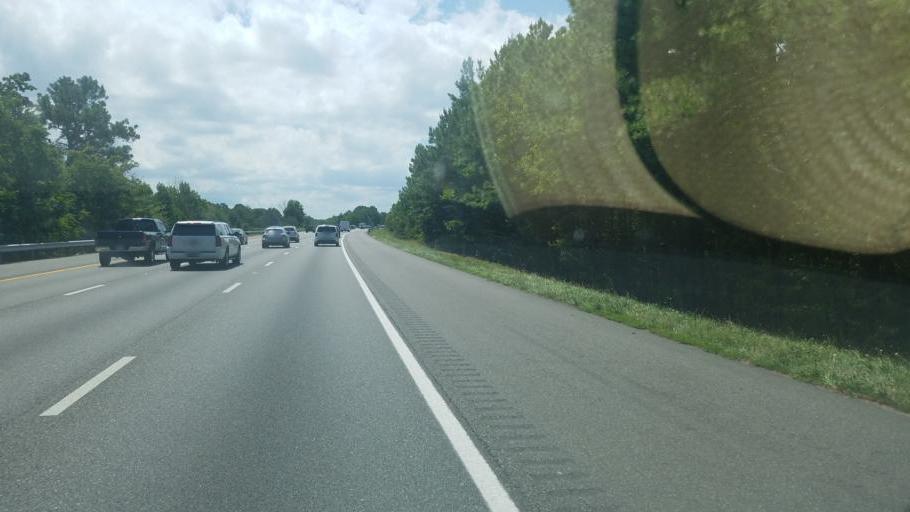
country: US
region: Virginia
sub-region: Hanover County
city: Ashland
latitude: 37.8629
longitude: -77.4536
